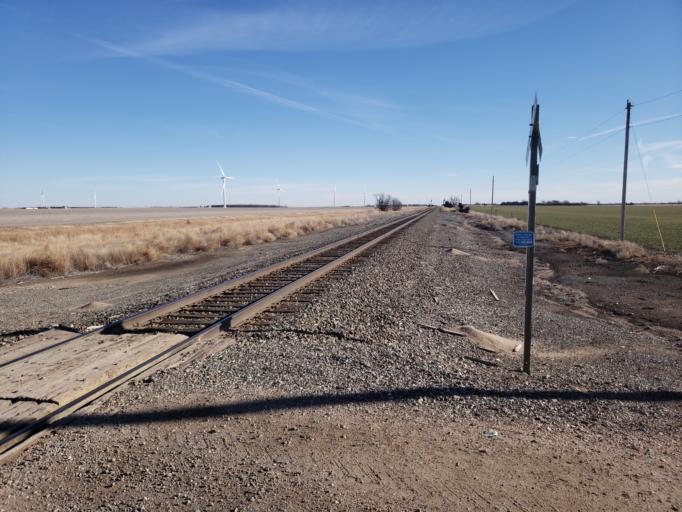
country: US
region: Kansas
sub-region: Edwards County
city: Kinsley
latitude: 37.8818
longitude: -99.6068
